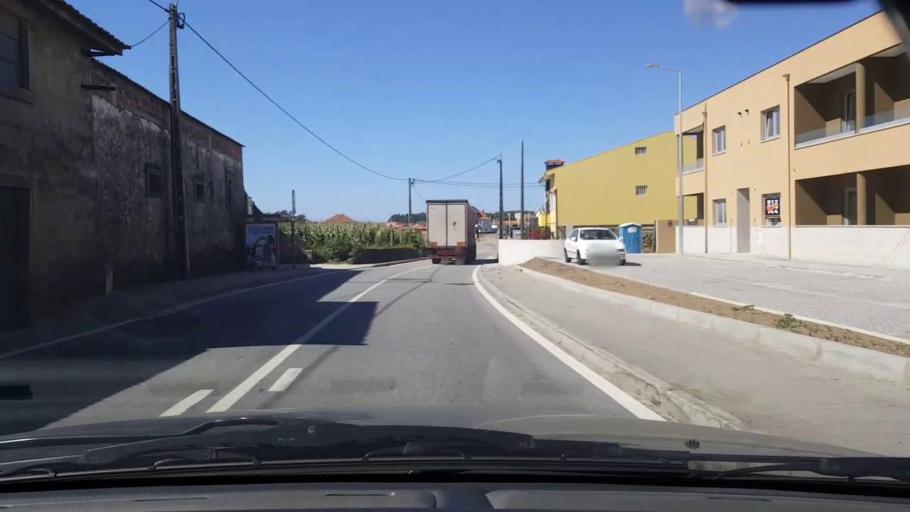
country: PT
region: Porto
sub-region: Vila do Conde
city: Arvore
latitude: 41.3406
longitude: -8.7013
